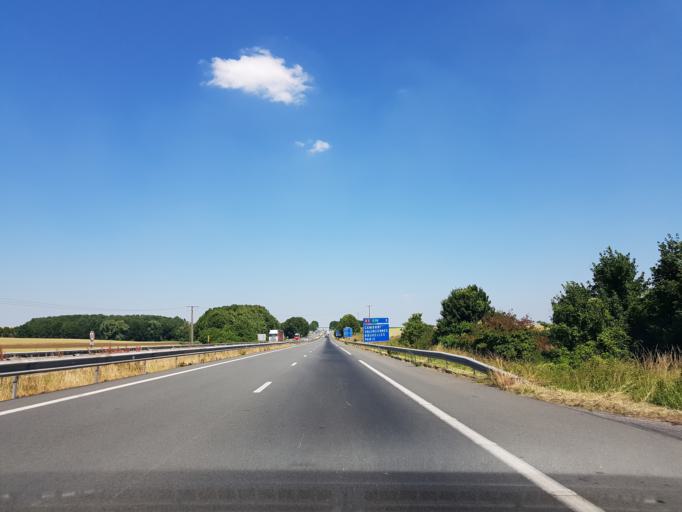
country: FR
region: Nord-Pas-de-Calais
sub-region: Departement du Nord
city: Marcoing
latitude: 50.0803
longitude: 3.1741
